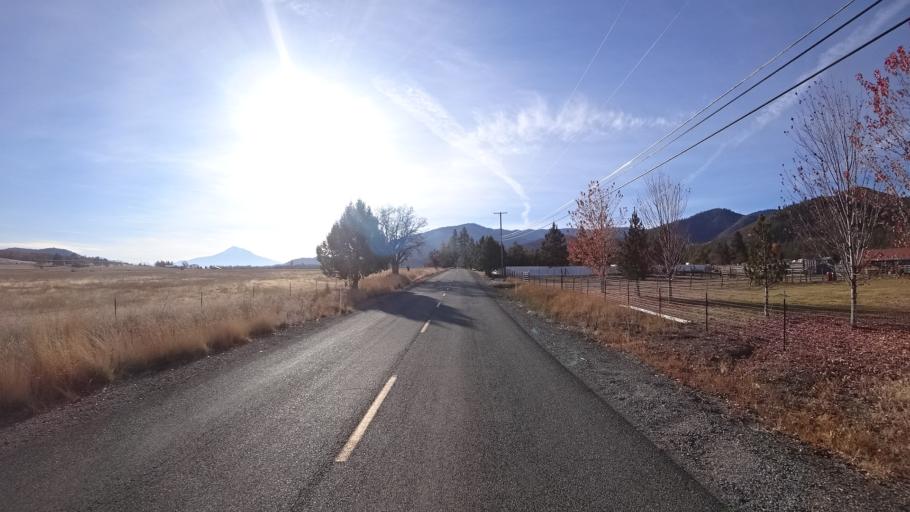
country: US
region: California
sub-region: Siskiyou County
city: Yreka
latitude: 41.6795
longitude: -122.6348
